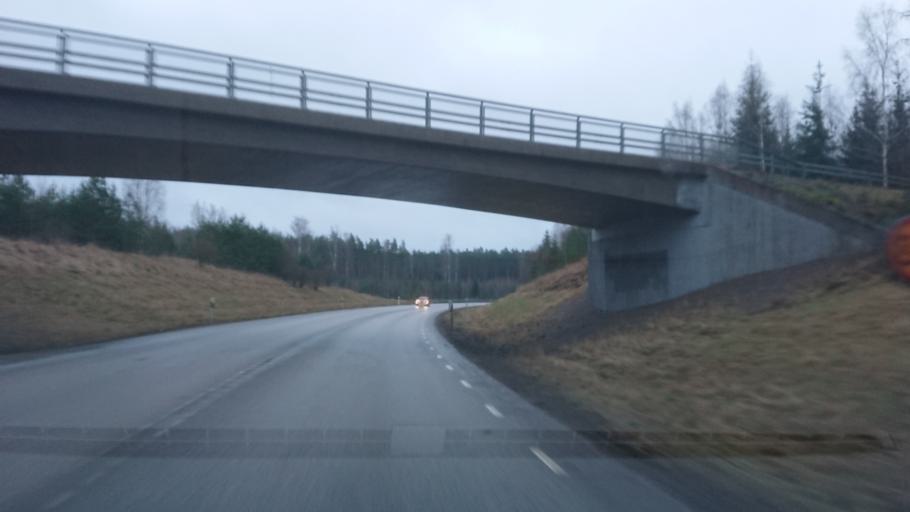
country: SE
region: Uppsala
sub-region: Osthammars Kommun
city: Bjorklinge
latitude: 60.0184
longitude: 17.5825
